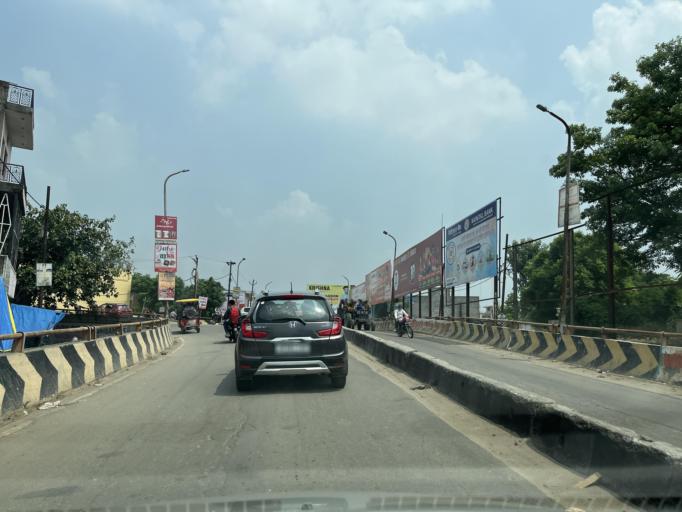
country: IN
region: Uttar Pradesh
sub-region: Bijnor
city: Najibabad
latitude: 29.6029
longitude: 78.3435
